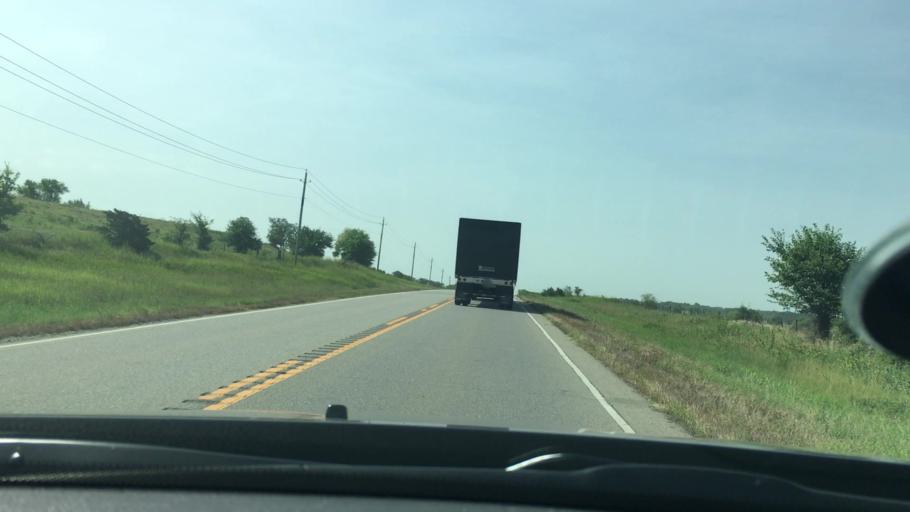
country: US
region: Oklahoma
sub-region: Coal County
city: Coalgate
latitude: 34.4587
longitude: -96.2144
